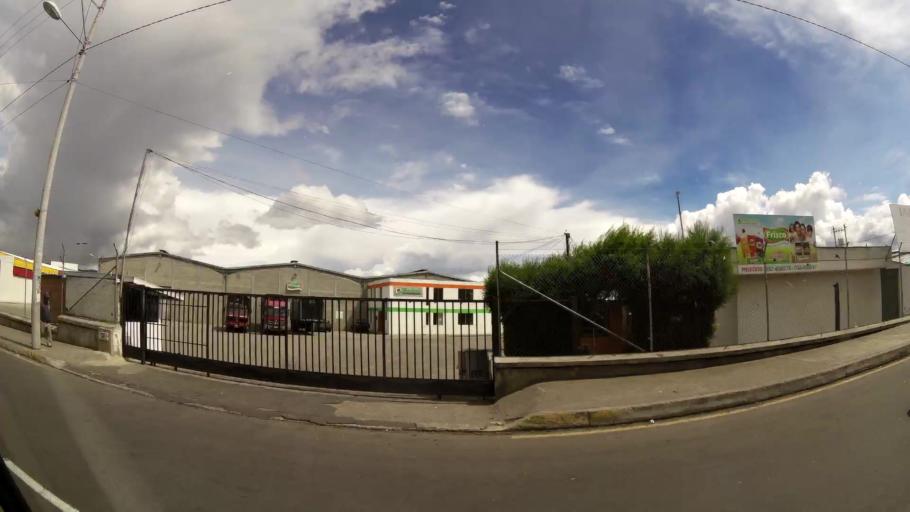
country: EC
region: Tungurahua
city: Ambato
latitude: -1.2684
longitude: -78.6131
